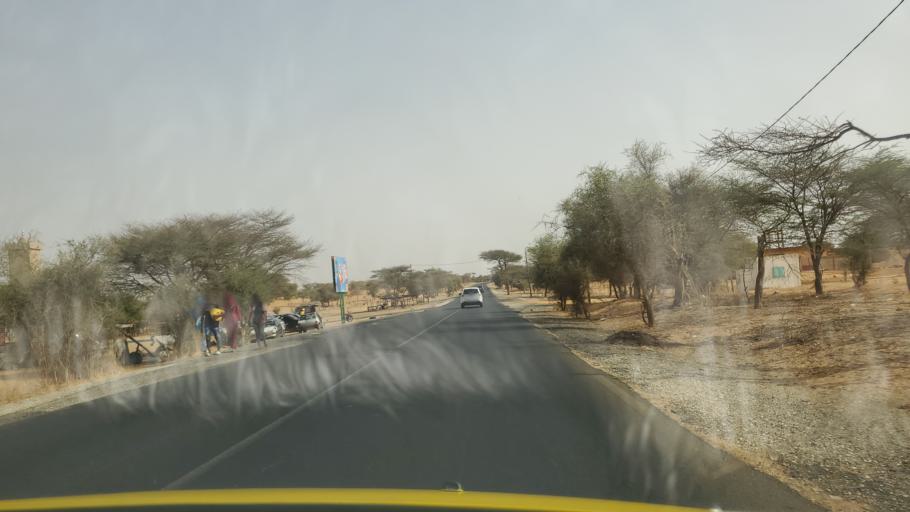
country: SN
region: Louga
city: Louga
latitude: 15.8447
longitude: -16.2336
